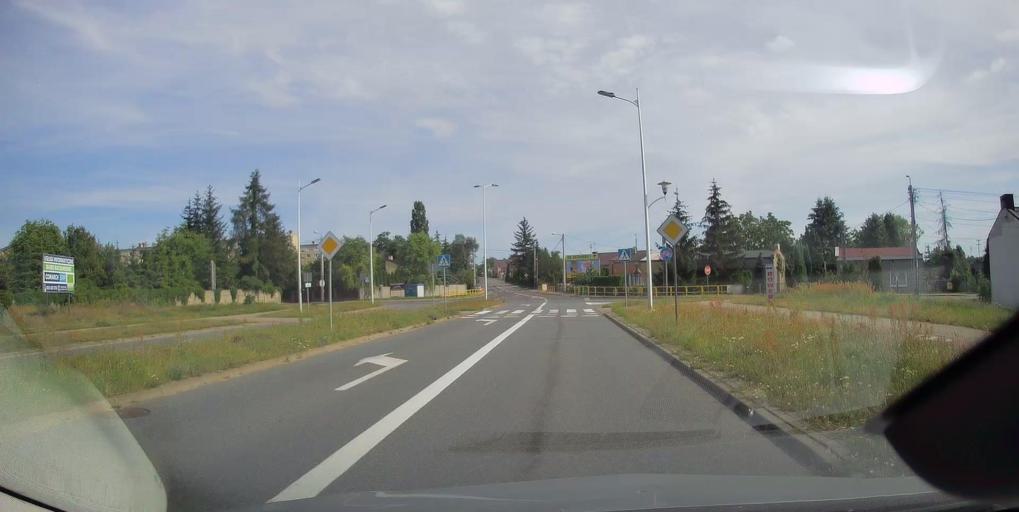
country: PL
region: Lodz Voivodeship
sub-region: Powiat tomaszowski
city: Tomaszow Mazowiecki
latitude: 51.5446
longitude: 19.9939
